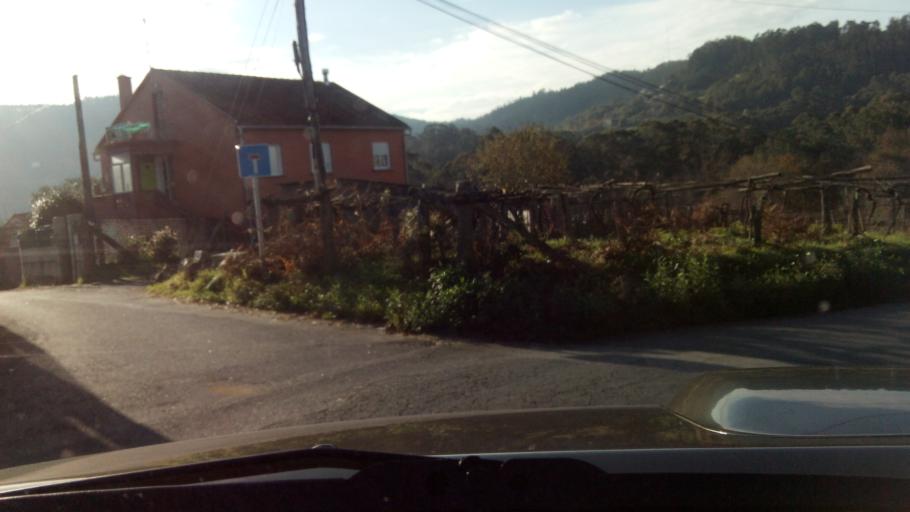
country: ES
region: Galicia
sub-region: Provincia de Pontevedra
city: Marin
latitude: 42.3614
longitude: -8.7089
